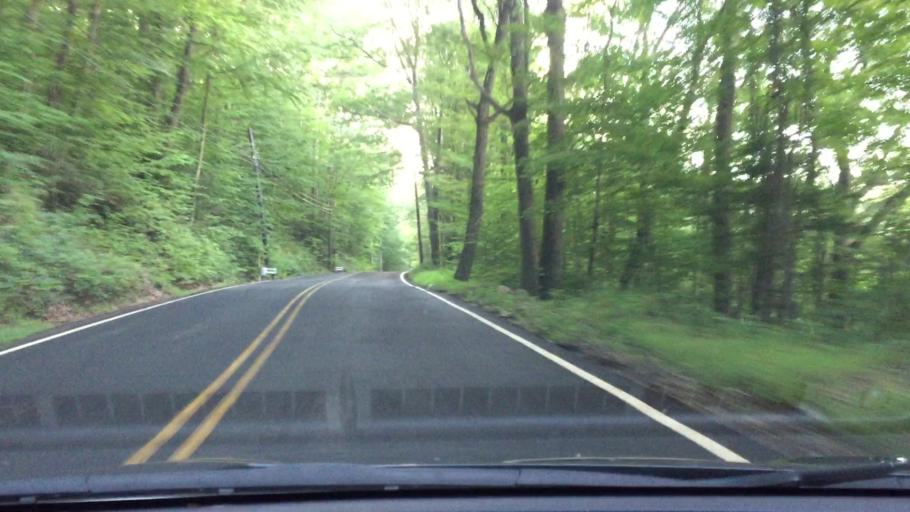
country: US
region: Massachusetts
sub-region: Hampden County
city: Westfield
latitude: 42.1971
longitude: -72.8469
